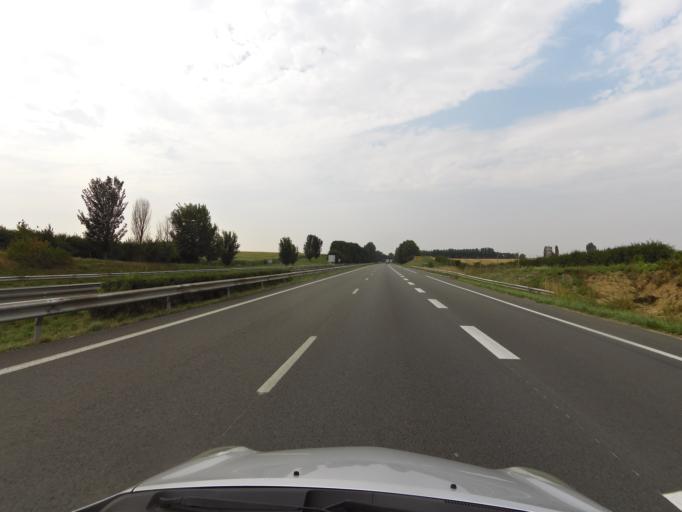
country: FR
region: Nord-Pas-de-Calais
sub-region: Departement du Pas-de-Calais
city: Bourlon
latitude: 50.1464
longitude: 3.1235
